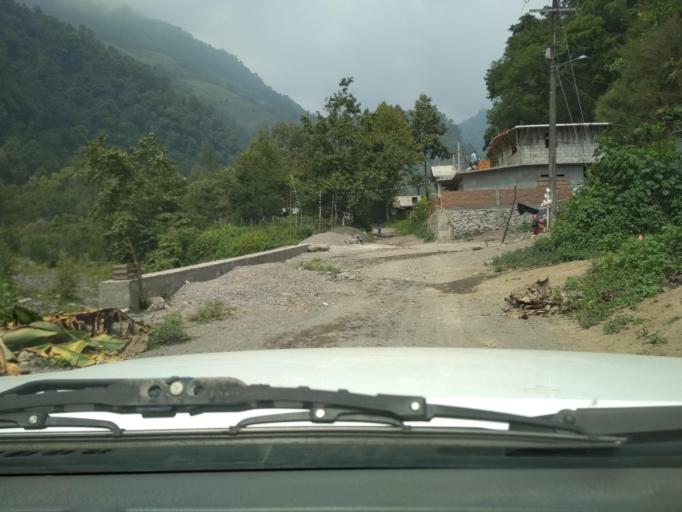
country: MX
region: Veracruz
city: Xocotla
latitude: 18.9890
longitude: -97.1120
